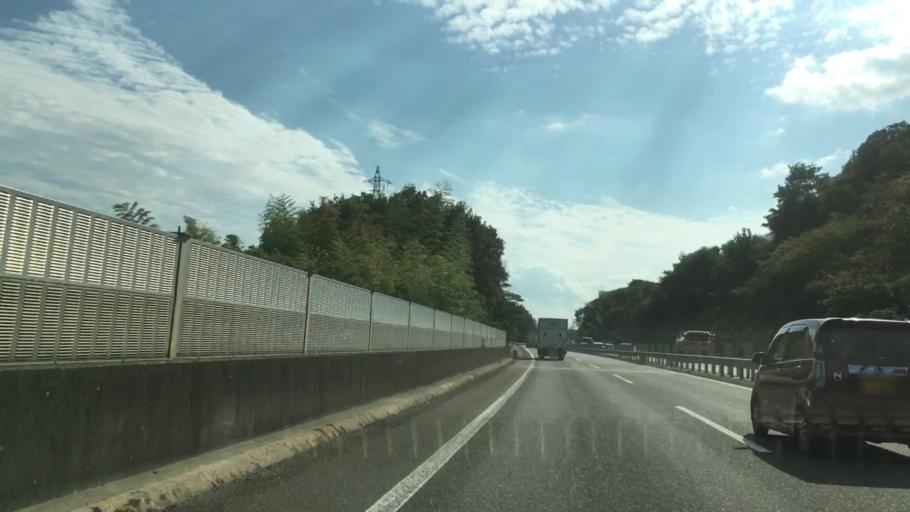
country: JP
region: Hiroshima
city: Ono-hara
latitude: 34.2828
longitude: 132.2603
